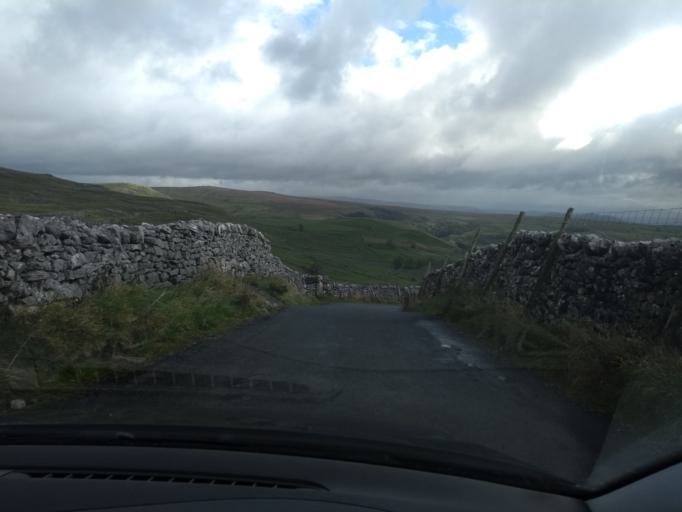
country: GB
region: England
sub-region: North Yorkshire
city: Gargrave
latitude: 54.0715
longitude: -2.1659
